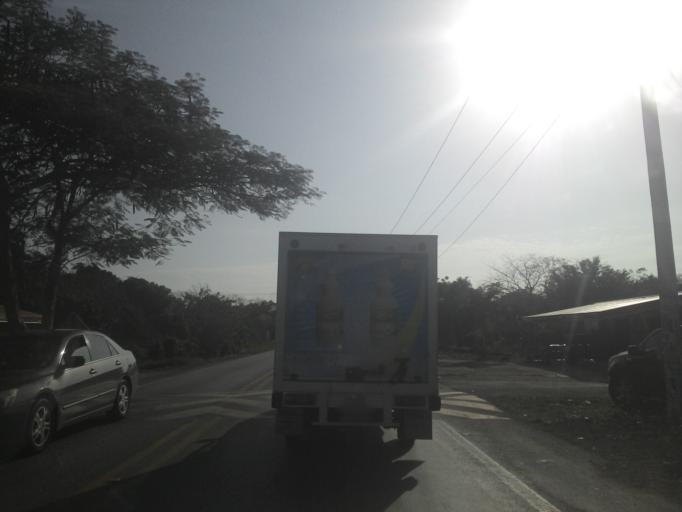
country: MX
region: Yucatan
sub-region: Valladolid
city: Tikuch
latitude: 20.7014
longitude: -88.1172
